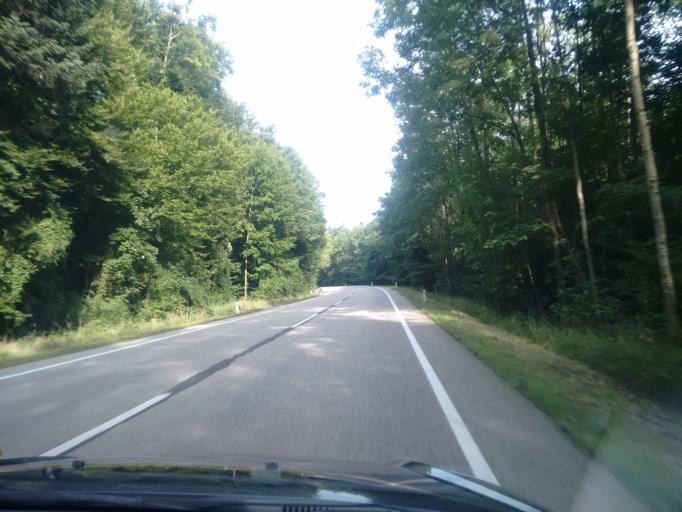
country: DE
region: Bavaria
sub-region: Upper Bavaria
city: Haiming
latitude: 48.2040
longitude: 12.9181
